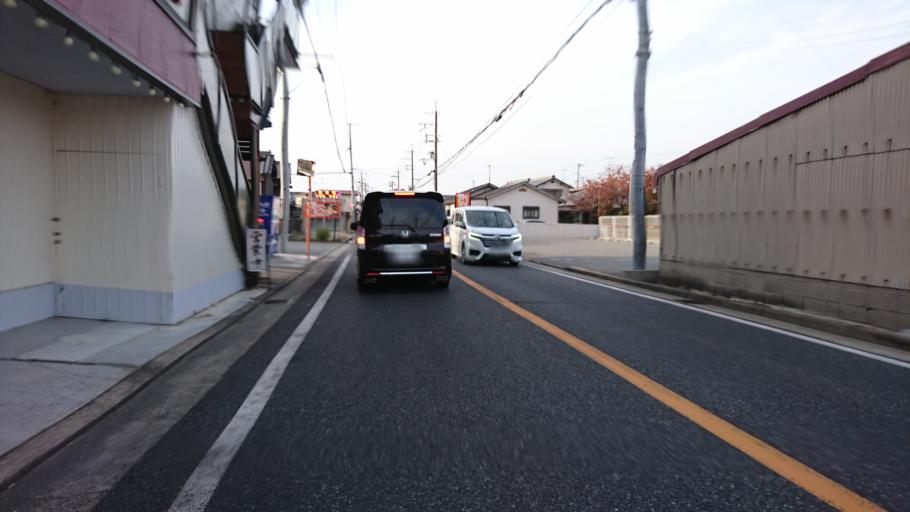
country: JP
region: Hyogo
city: Kakogawacho-honmachi
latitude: 34.7374
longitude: 134.8272
